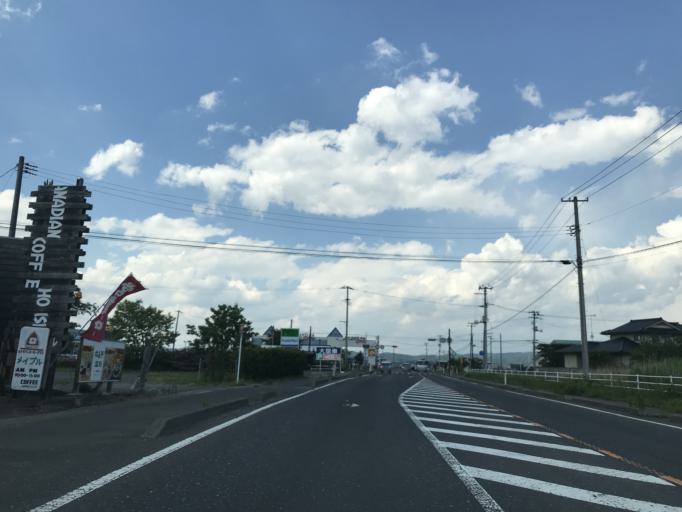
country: JP
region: Miyagi
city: Wakuya
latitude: 38.5075
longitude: 141.1209
